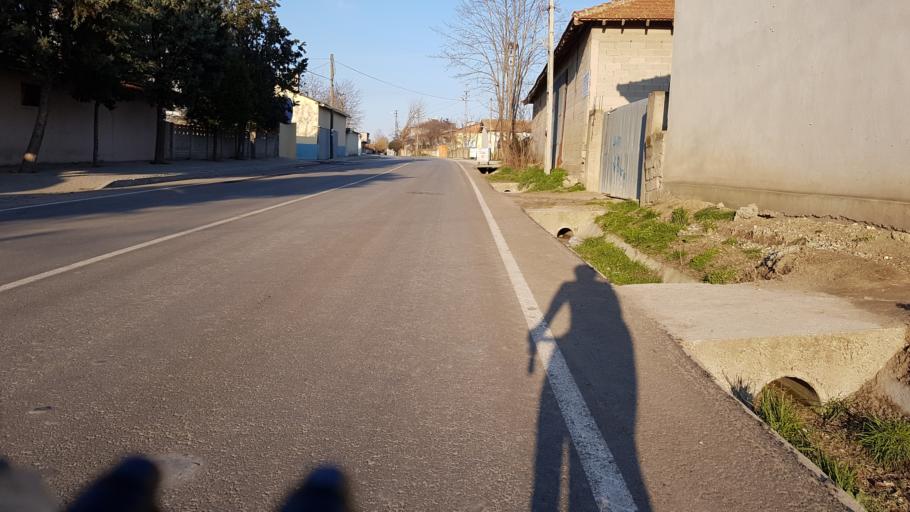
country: TR
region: Tekirdag
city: Beyazkoy
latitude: 41.3035
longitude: 27.7853
